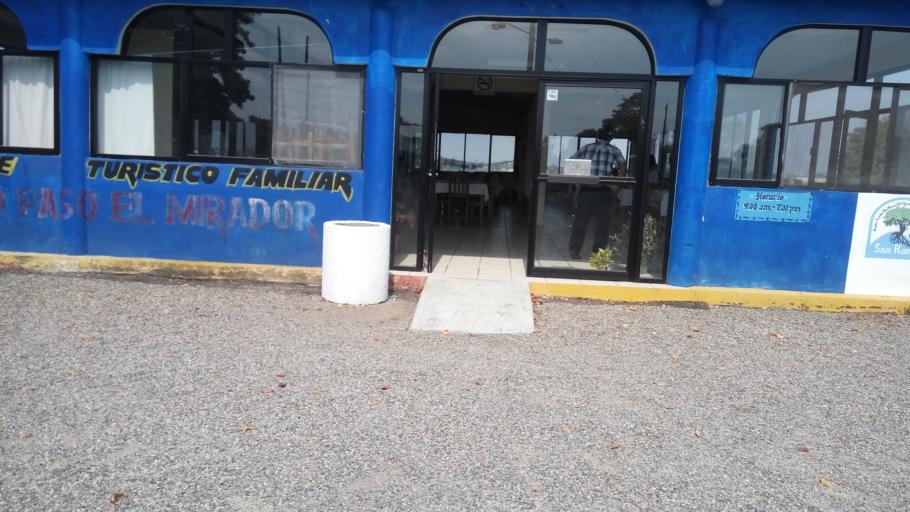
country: MX
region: Tabasco
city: Frontera
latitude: 18.5179
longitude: -92.6602
